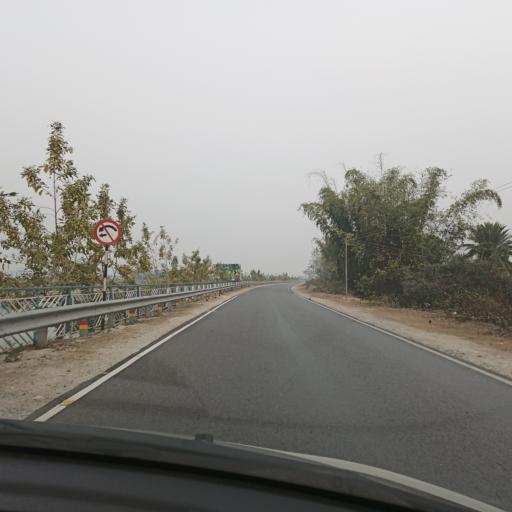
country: IN
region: West Bengal
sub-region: Jalpaiguri
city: Odlabari
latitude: 26.7356
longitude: 88.5753
